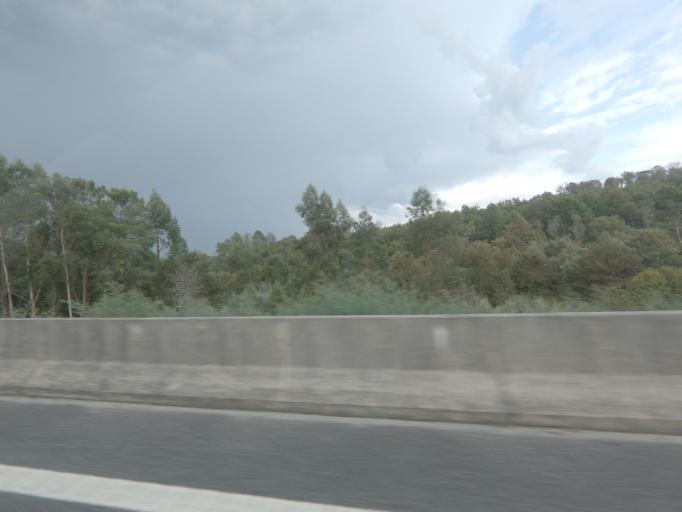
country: PT
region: Viseu
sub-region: Viseu
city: Abraveses
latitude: 40.6541
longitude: -7.9665
